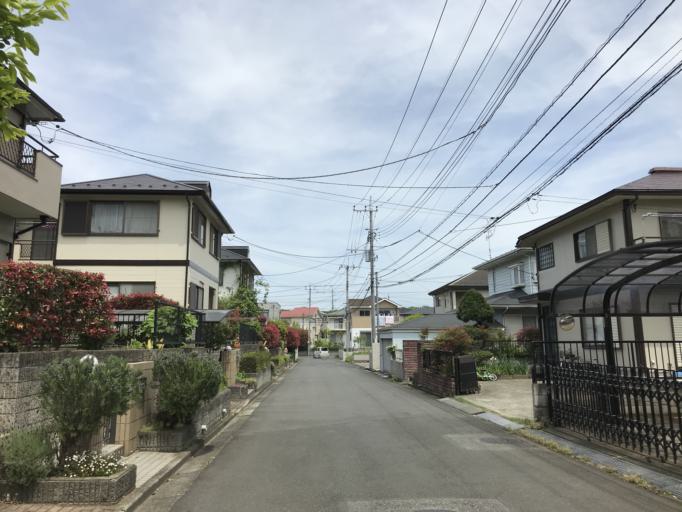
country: JP
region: Ibaraki
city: Mitsukaido
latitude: 35.9711
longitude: 139.9577
